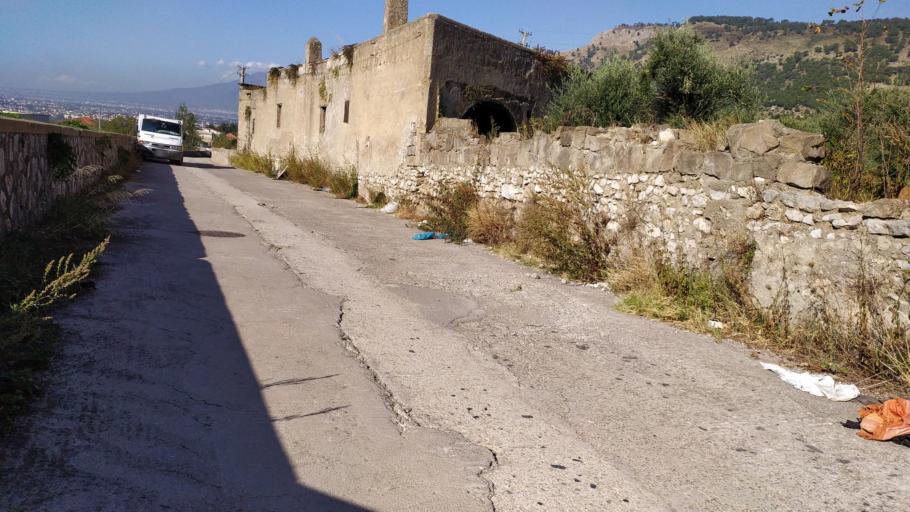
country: IT
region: Campania
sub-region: Provincia di Salerno
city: Sarno
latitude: 40.8035
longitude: 14.6516
